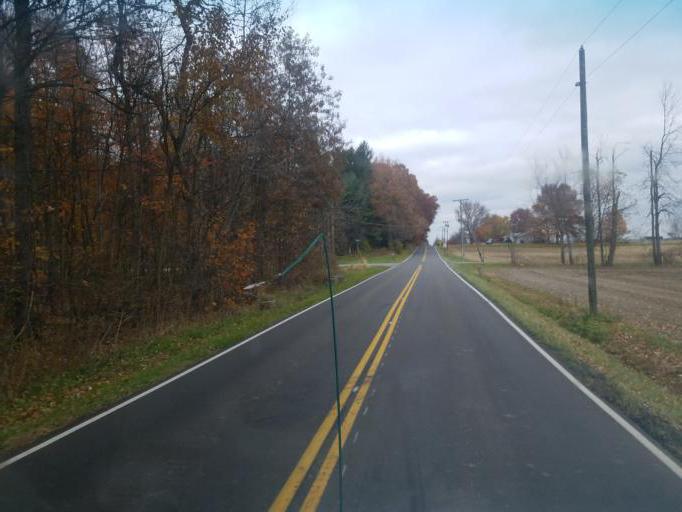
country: US
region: Ohio
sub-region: Richland County
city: Shelby
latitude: 40.8277
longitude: -82.6291
